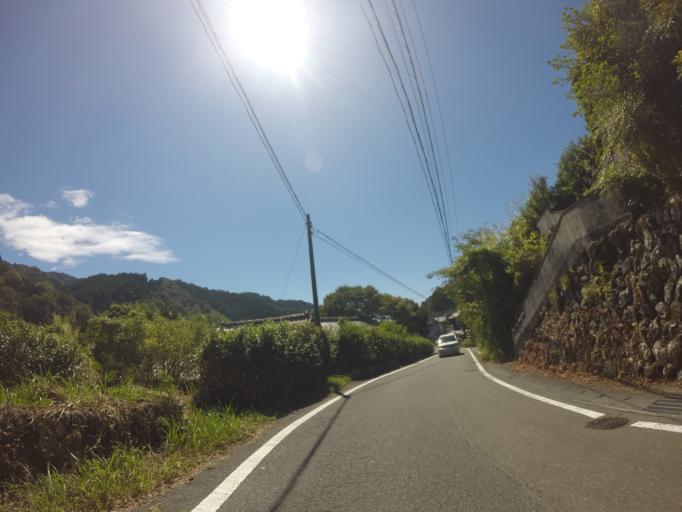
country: JP
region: Shizuoka
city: Fujieda
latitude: 34.9684
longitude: 138.2125
